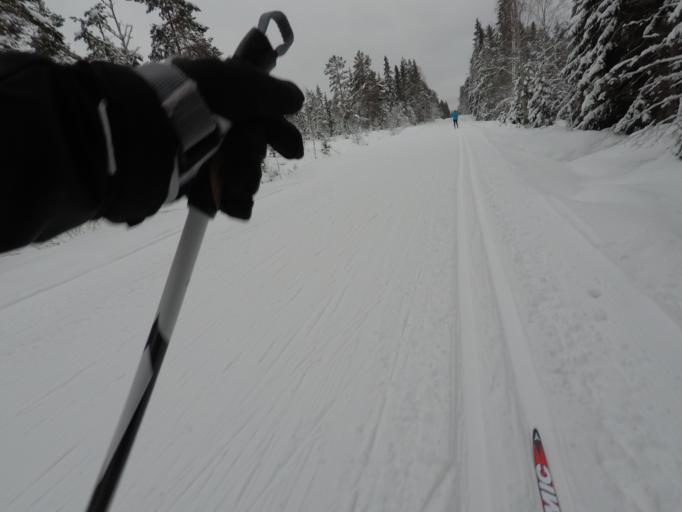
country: SE
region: Dalarna
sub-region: Ludvika Kommun
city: Abborrberget
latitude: 60.1540
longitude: 14.4895
